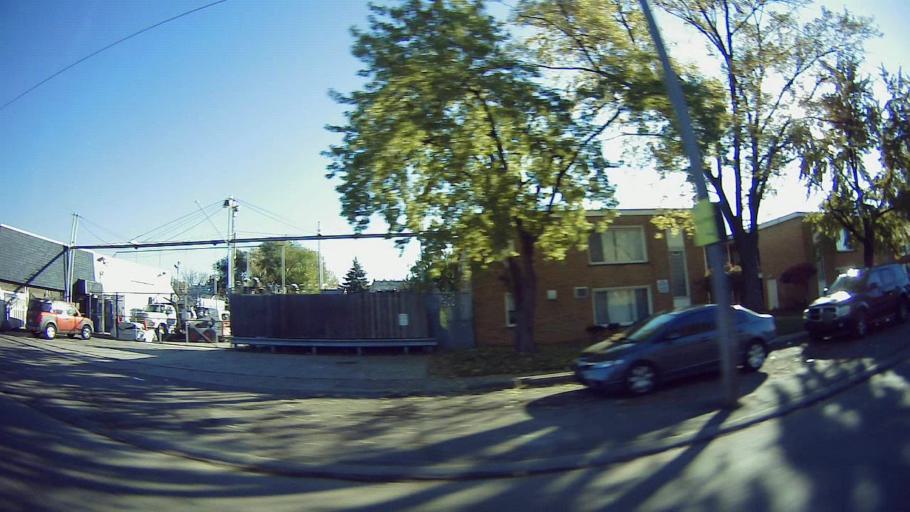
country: US
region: Michigan
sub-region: Oakland County
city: Oak Park
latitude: 42.4115
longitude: -83.1991
